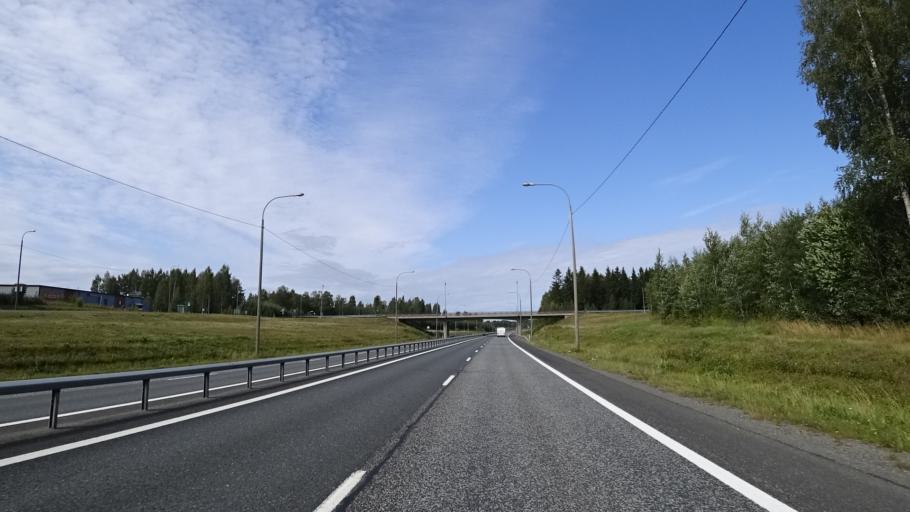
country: FI
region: North Karelia
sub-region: Joensuu
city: Joensuu
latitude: 62.5424
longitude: 29.8480
